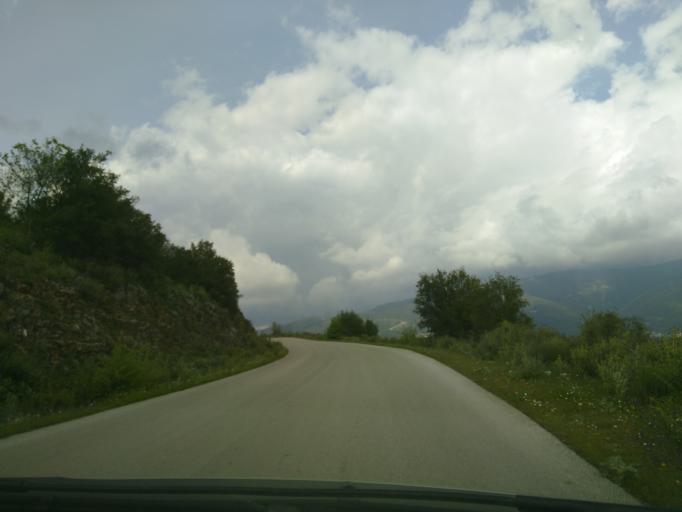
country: GR
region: Epirus
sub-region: Nomos Ioanninon
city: Asprangeloi
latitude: 39.7718
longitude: 20.6995
